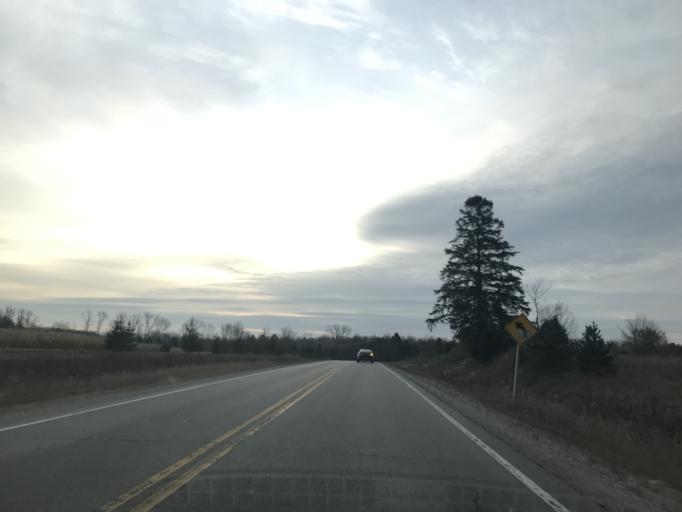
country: US
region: Wisconsin
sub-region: Marinette County
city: Peshtigo
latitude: 45.0603
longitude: -87.7969
